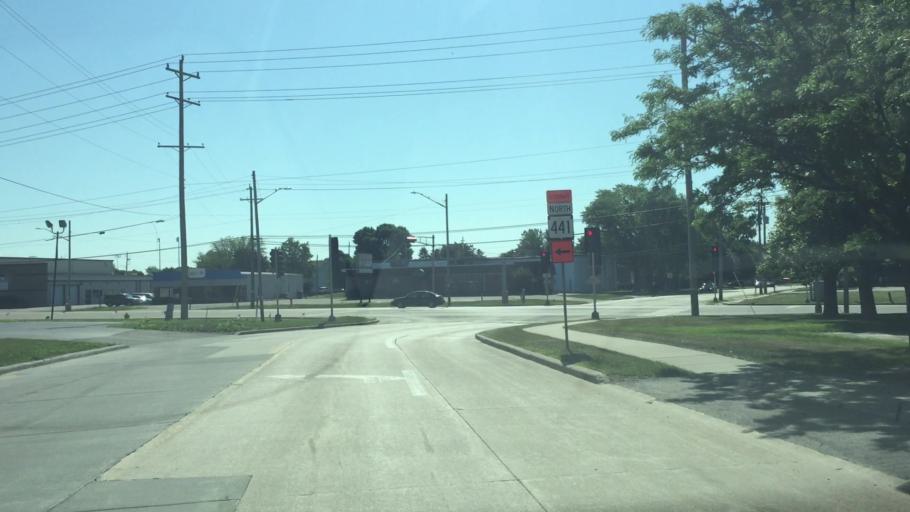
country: US
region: Wisconsin
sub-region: Winnebago County
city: Menasha
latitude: 44.2226
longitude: -88.4282
